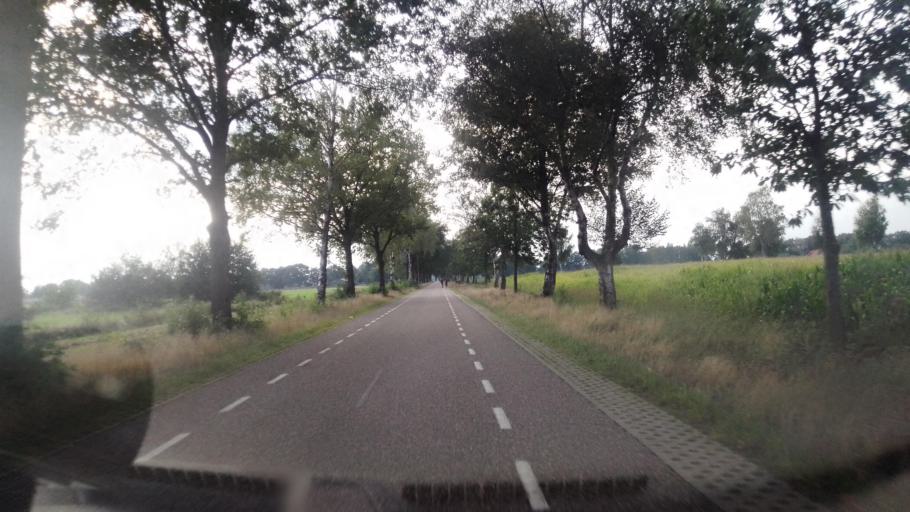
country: NL
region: Limburg
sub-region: Gemeente Peel en Maas
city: Maasbree
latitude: 51.3947
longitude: 5.9618
